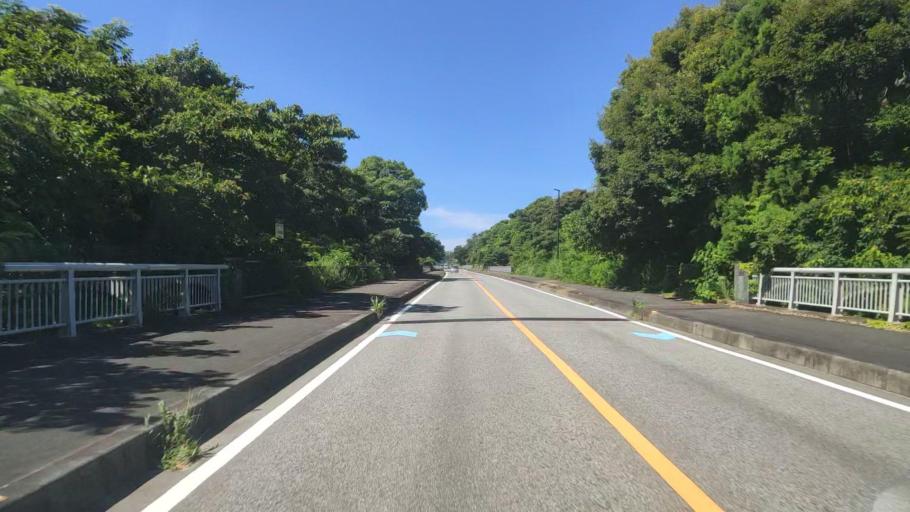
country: JP
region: Wakayama
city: Shingu
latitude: 33.7103
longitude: 135.9973
